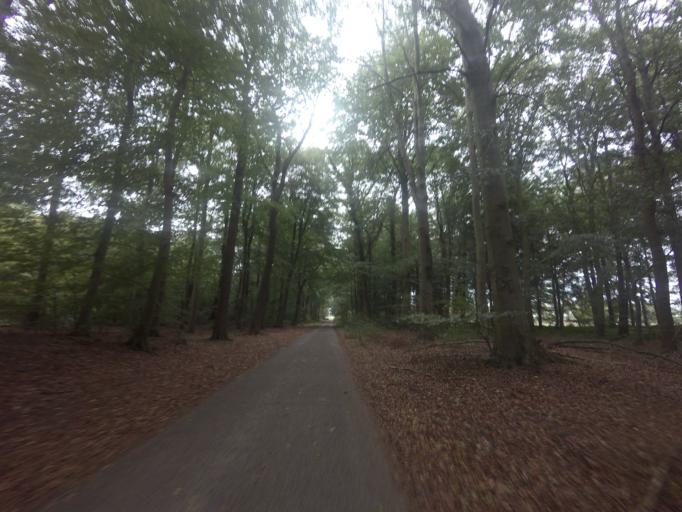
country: NL
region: Drenthe
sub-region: Gemeente Westerveld
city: Dwingeloo
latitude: 52.9506
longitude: 6.3116
